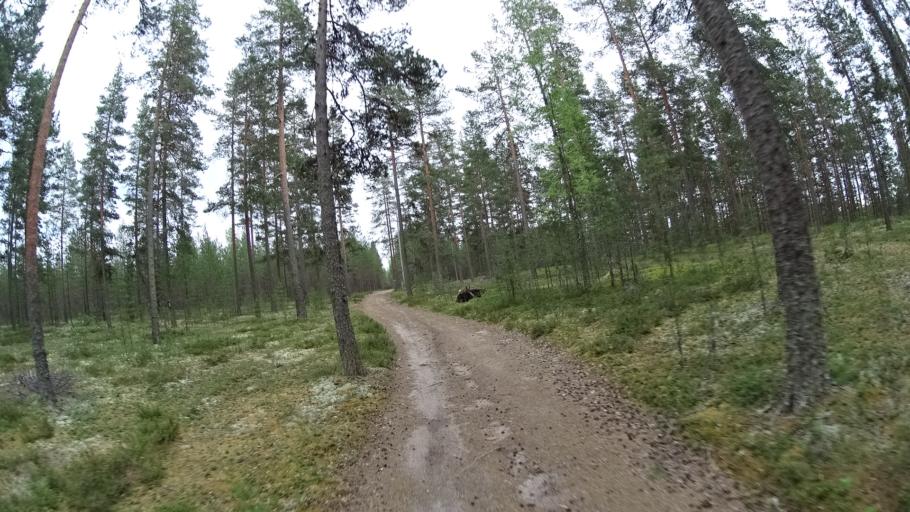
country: FI
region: Satakunta
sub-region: Pohjois-Satakunta
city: Jaemijaervi
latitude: 61.7632
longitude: 22.7708
